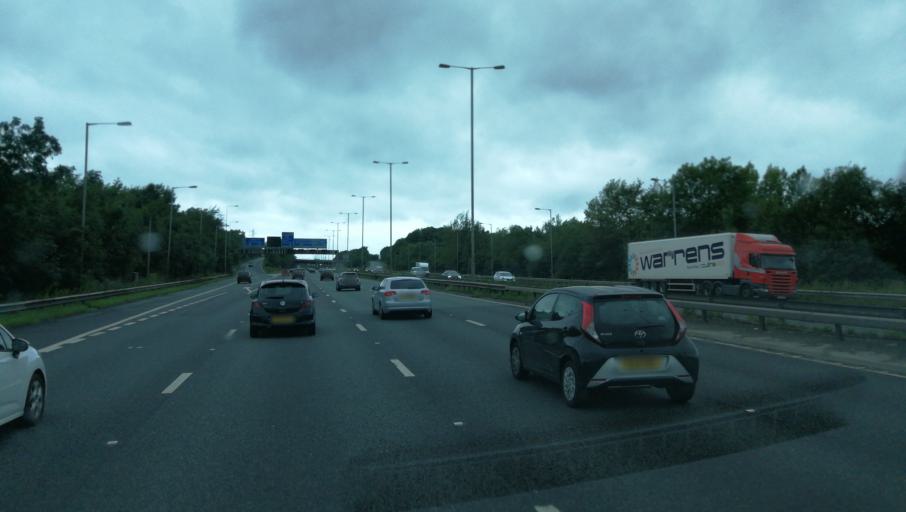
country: GB
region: England
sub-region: Borough of Bury
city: Radcliffe
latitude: 53.5283
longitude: -2.3270
